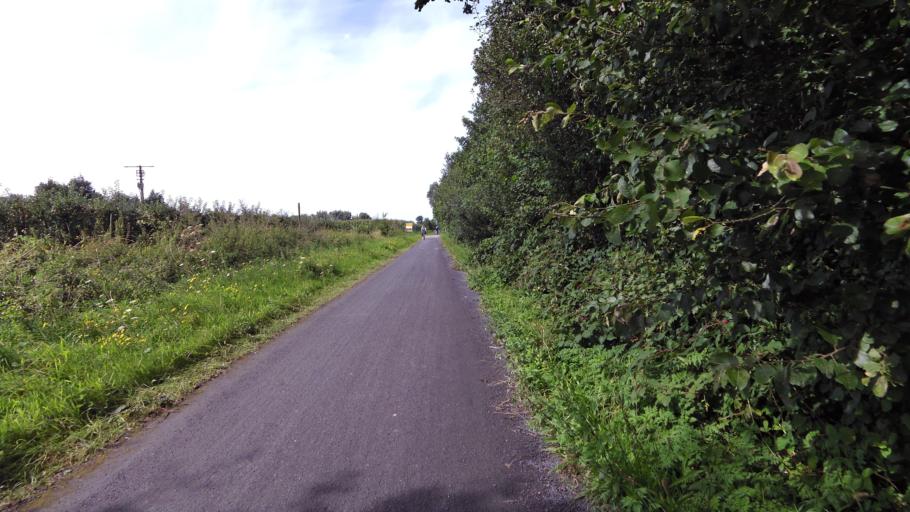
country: BE
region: Flanders
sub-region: Provincie West-Vlaanderen
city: Ichtegem
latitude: 51.1180
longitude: 3.0301
